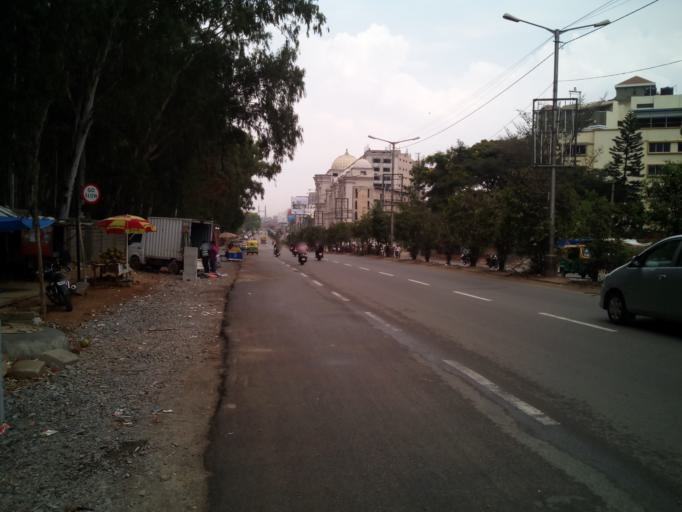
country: IN
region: Karnataka
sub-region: Bangalore Urban
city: Bangalore
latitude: 12.9917
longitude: 77.6580
